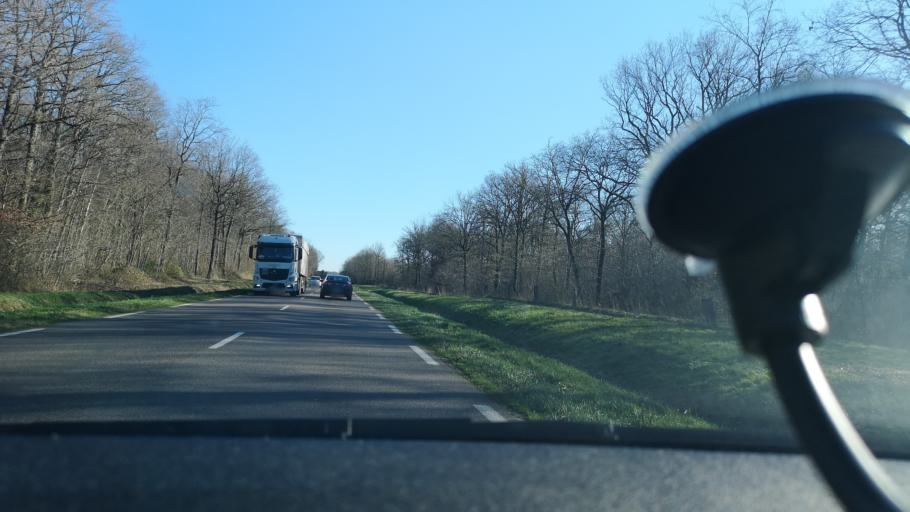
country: FR
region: Bourgogne
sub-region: Departement de Saone-et-Loire
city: Ouroux-sur-Saone
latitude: 46.7761
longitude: 4.9569
